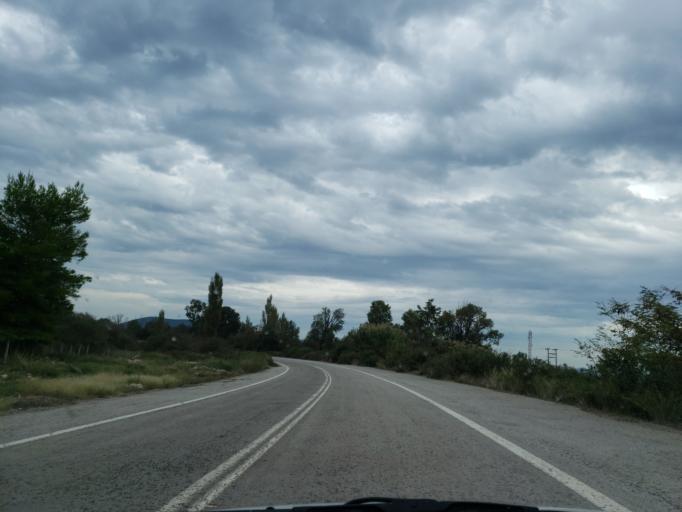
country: GR
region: Central Greece
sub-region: Nomos Voiotias
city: Akraifnia
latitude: 38.4578
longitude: 23.1640
